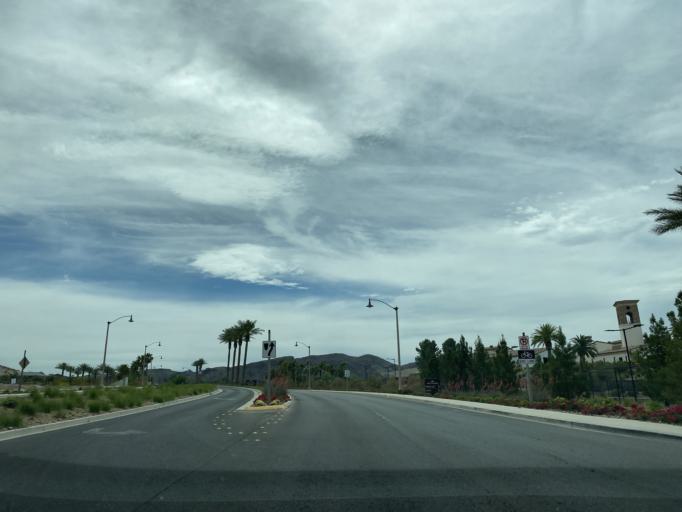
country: US
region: Nevada
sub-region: Clark County
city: Henderson
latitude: 36.0886
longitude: -114.9315
